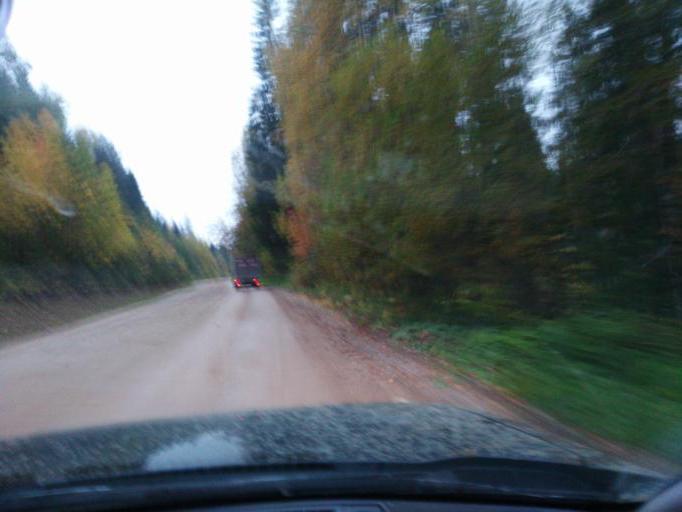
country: RU
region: Sverdlovsk
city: Sylva
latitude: 57.7987
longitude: 58.5741
